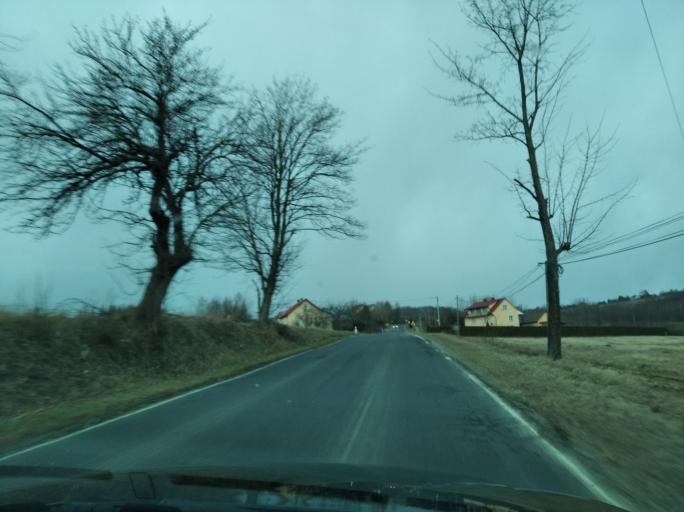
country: PL
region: Subcarpathian Voivodeship
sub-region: Powiat rzeszowski
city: Hyzne
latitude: 49.9137
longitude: 22.1991
